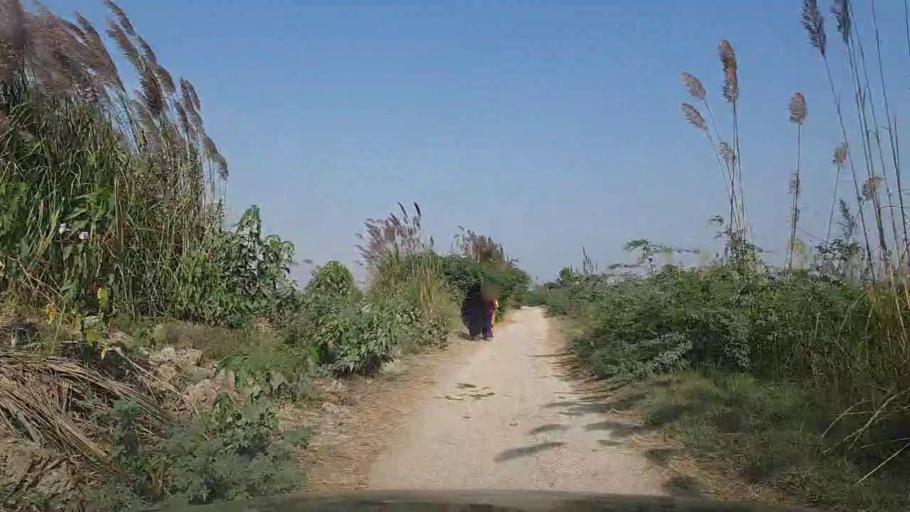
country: PK
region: Sindh
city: Thatta
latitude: 24.7820
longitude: 67.8078
